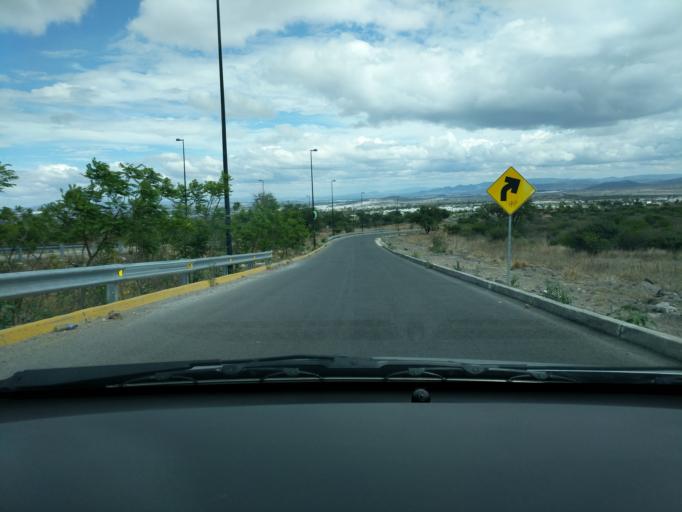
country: MX
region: Queretaro
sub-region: El Marques
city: La Pradera
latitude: 20.6690
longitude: -100.3171
